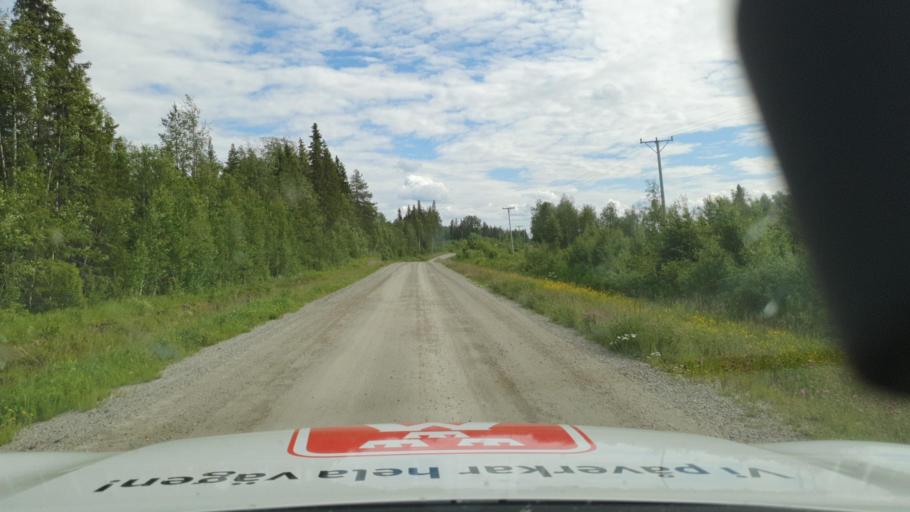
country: SE
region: Vaesterbotten
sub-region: Norsjo Kommun
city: Norsjoe
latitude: 64.8684
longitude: 19.4826
